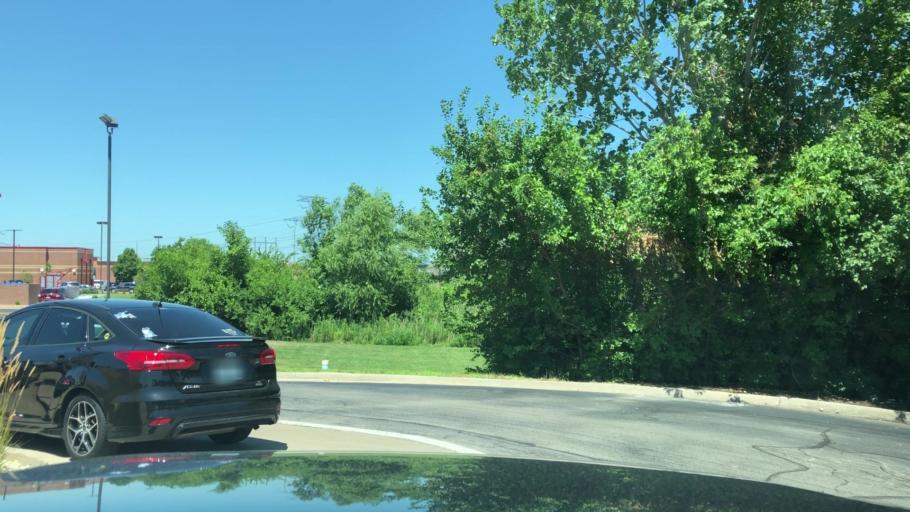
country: US
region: Missouri
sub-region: Saint Charles County
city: Saint Charles
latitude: 38.8207
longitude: -90.5135
